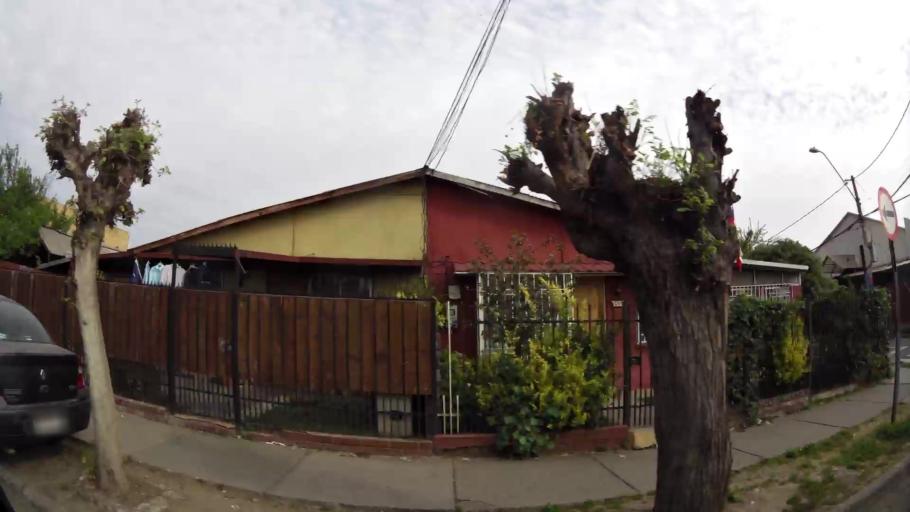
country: CL
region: Santiago Metropolitan
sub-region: Provincia de Santiago
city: Lo Prado
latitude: -33.5141
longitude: -70.7525
